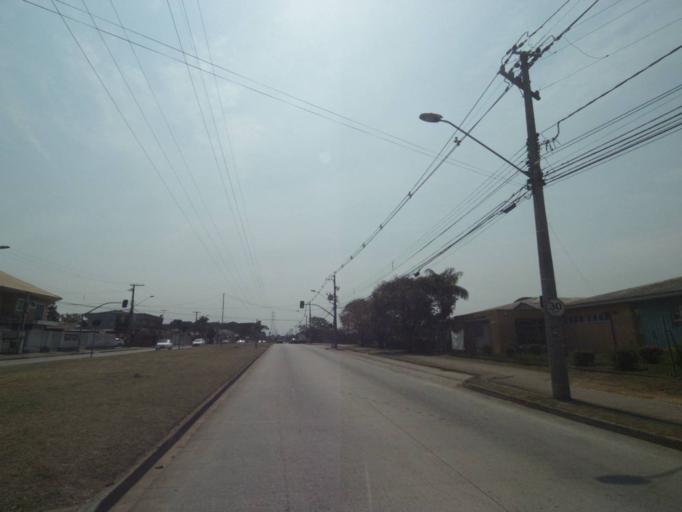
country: BR
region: Parana
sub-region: Sao Jose Dos Pinhais
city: Sao Jose dos Pinhais
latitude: -25.4958
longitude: -49.2089
